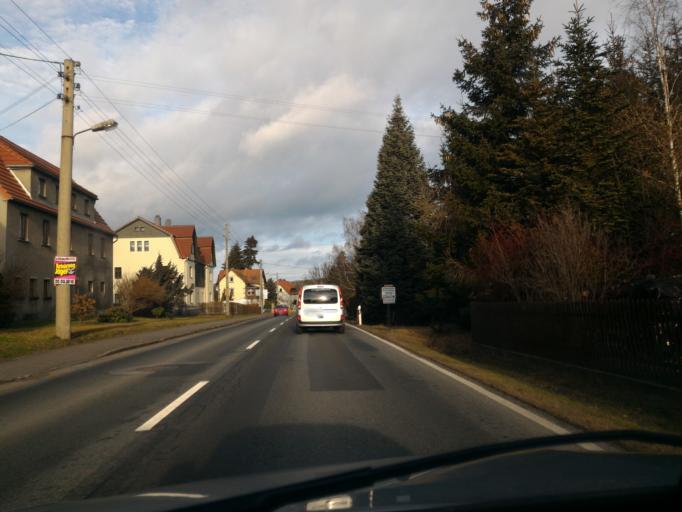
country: DE
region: Saxony
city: Friedersdorf
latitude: 51.0282
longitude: 14.5563
